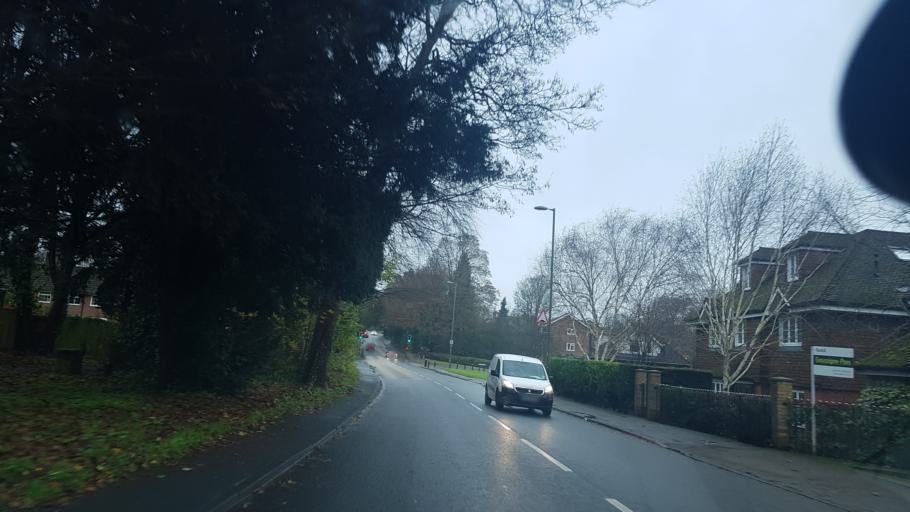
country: GB
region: England
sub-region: Surrey
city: Great Bookham
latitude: 51.2772
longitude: -0.3739
